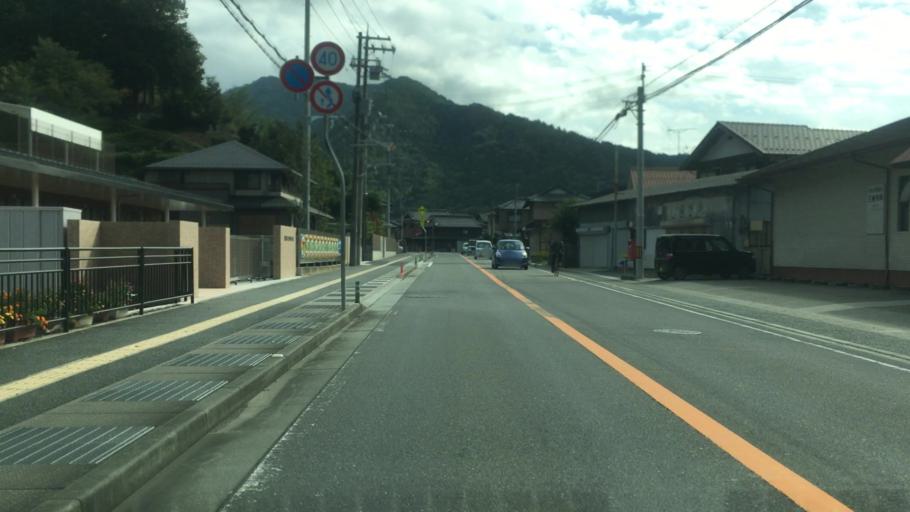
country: JP
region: Kyoto
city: Fukuchiyama
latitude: 35.1500
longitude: 135.0582
